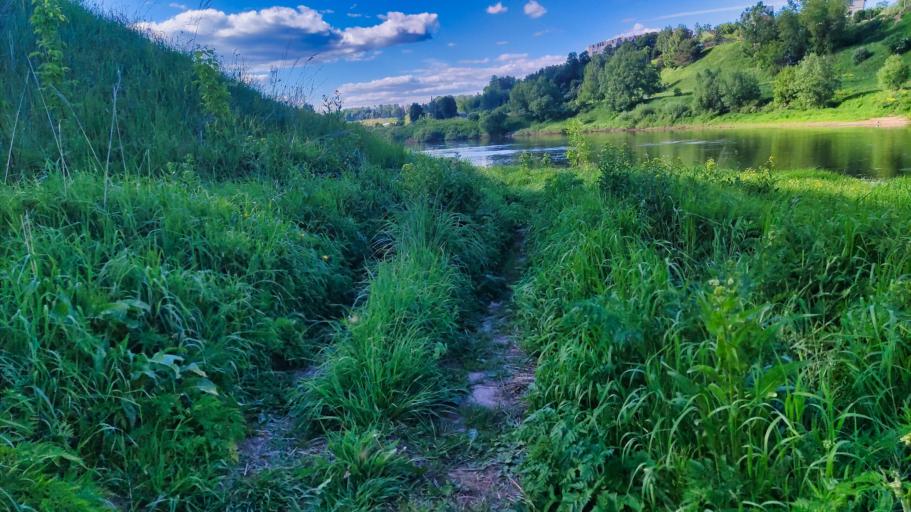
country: RU
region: Tverskaya
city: Rzhev
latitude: 56.2511
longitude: 34.3473
